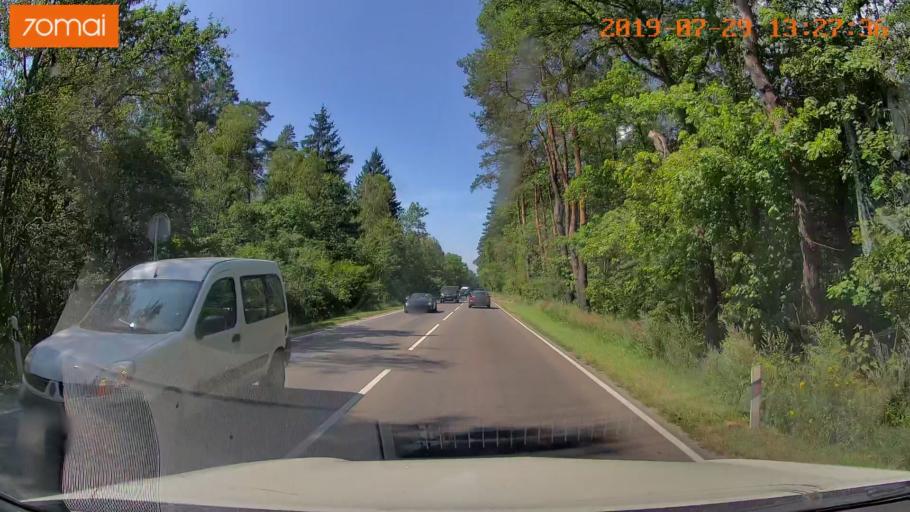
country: RU
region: Kaliningrad
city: Vzmorye
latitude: 54.7047
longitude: 20.2968
